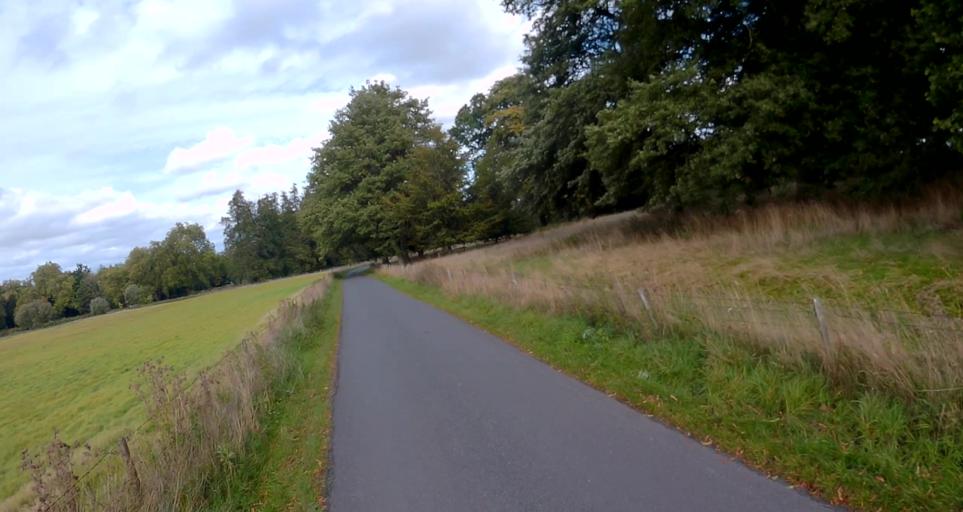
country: GB
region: England
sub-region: Hampshire
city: Kings Worthy
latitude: 51.0900
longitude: -1.2314
